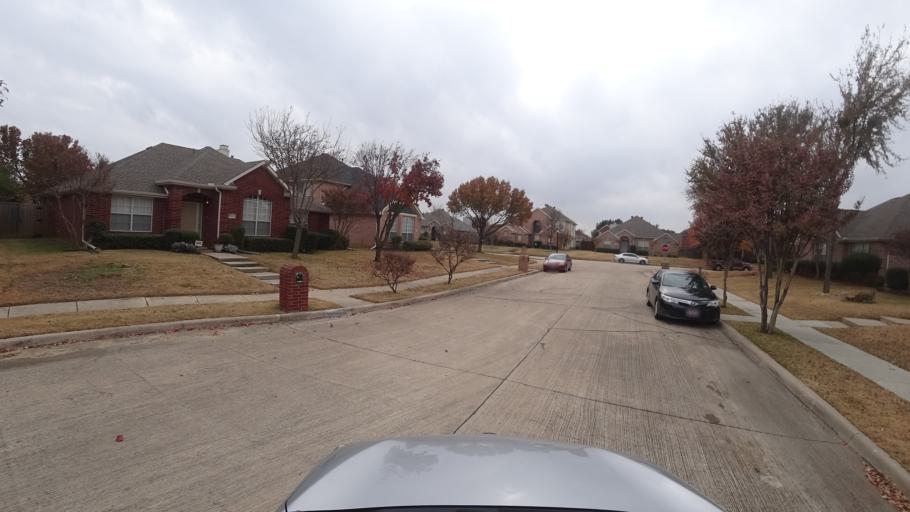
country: US
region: Texas
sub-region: Denton County
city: Lewisville
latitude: 33.0211
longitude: -96.9389
